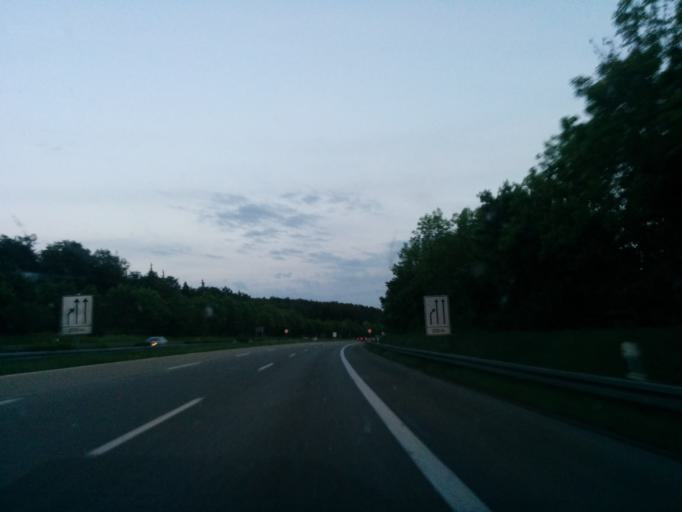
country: DE
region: Baden-Wuerttemberg
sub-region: Regierungsbezirk Stuttgart
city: Westhausen
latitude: 48.8565
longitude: 10.1975
